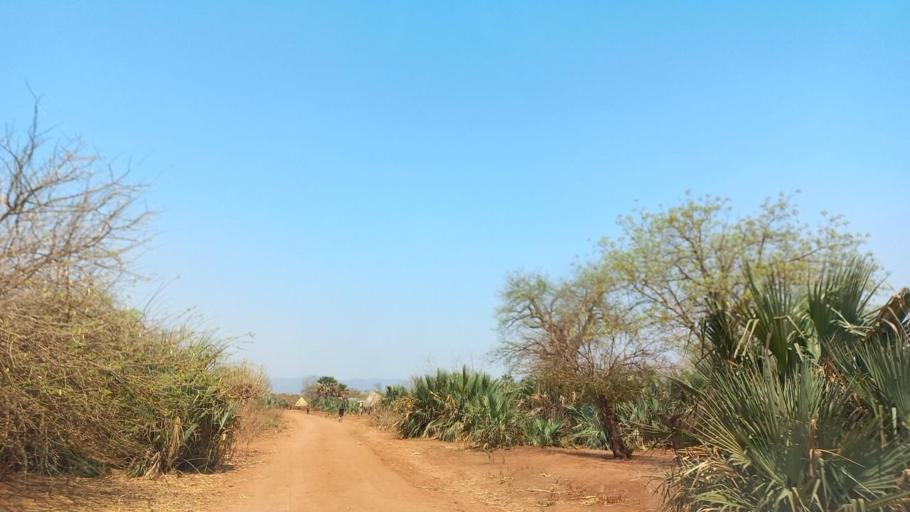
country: ZM
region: Lusaka
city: Luangwa
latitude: -15.1871
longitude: 30.2084
